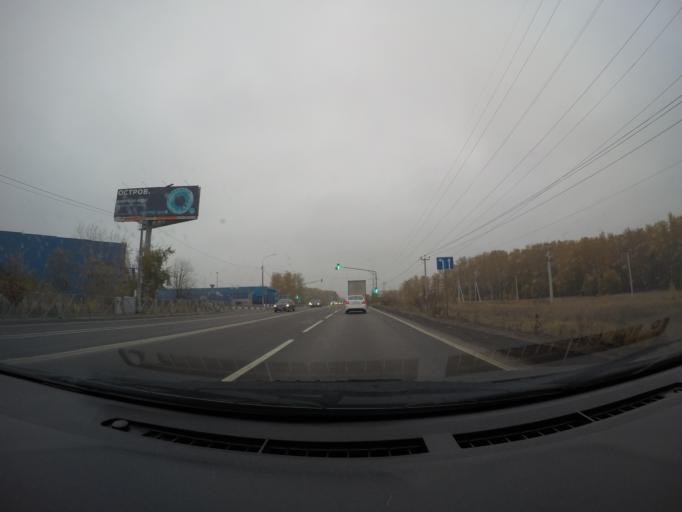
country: RU
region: Moskovskaya
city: Shcherbinka
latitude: 55.4882
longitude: 37.5977
